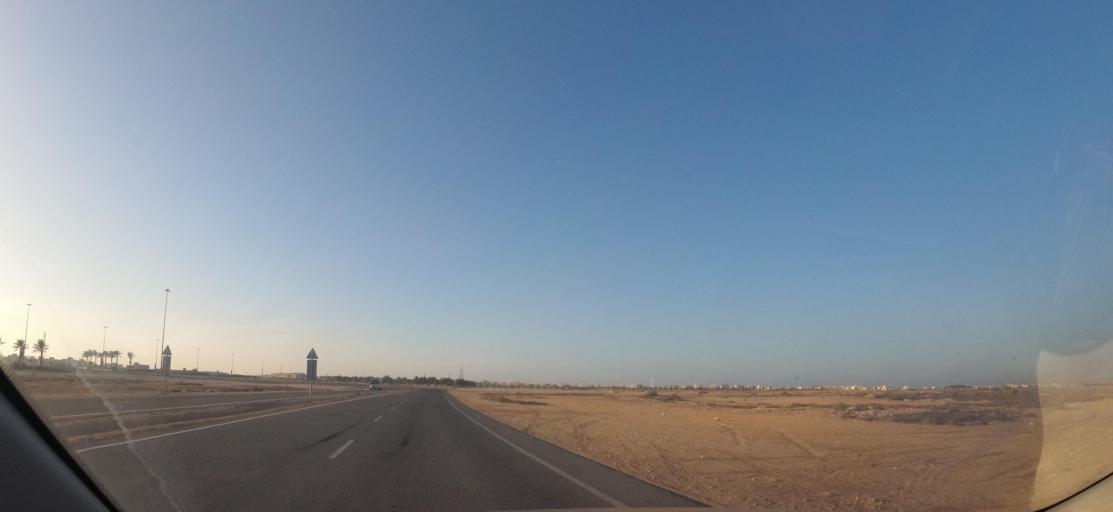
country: QA
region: Madinat ash Shamal
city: Ar Ru'ays
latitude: 26.1183
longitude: 51.2183
